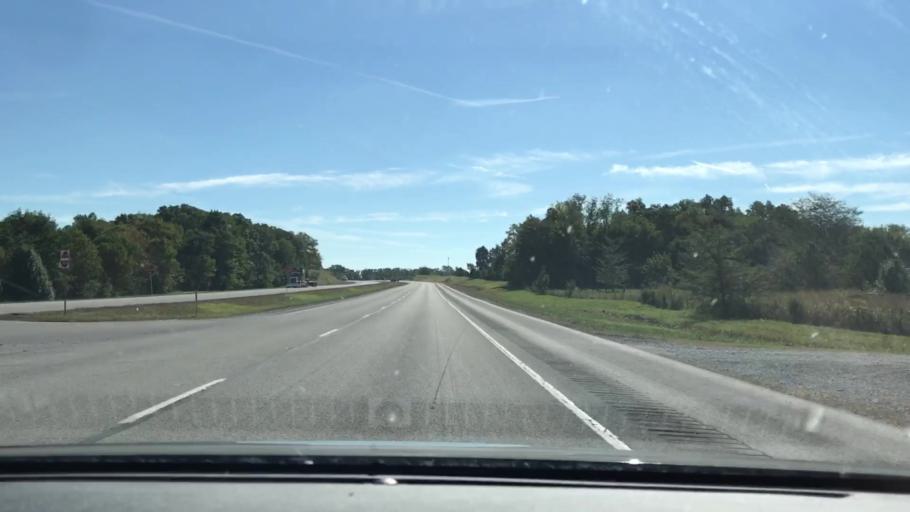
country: US
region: Kentucky
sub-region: Todd County
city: Elkton
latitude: 36.8300
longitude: -87.2266
